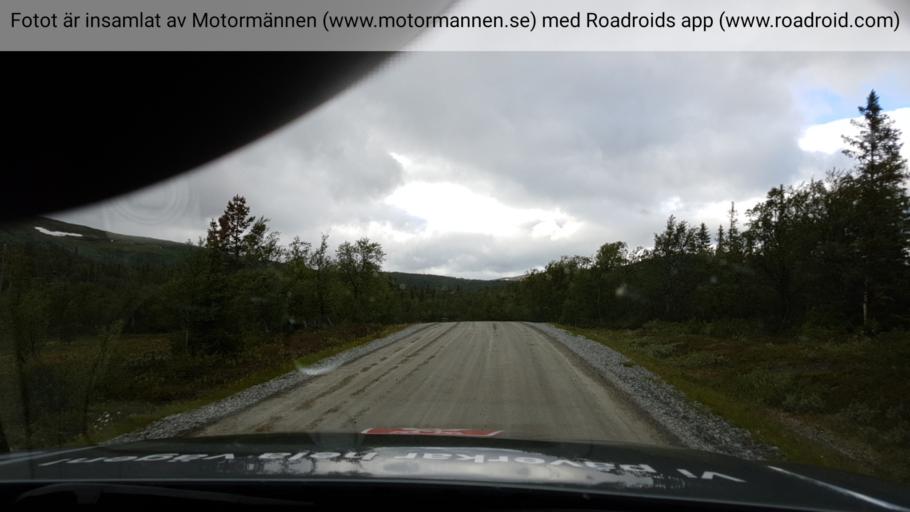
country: SE
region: Jaemtland
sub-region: Are Kommun
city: Are
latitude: 62.8773
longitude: 12.7337
